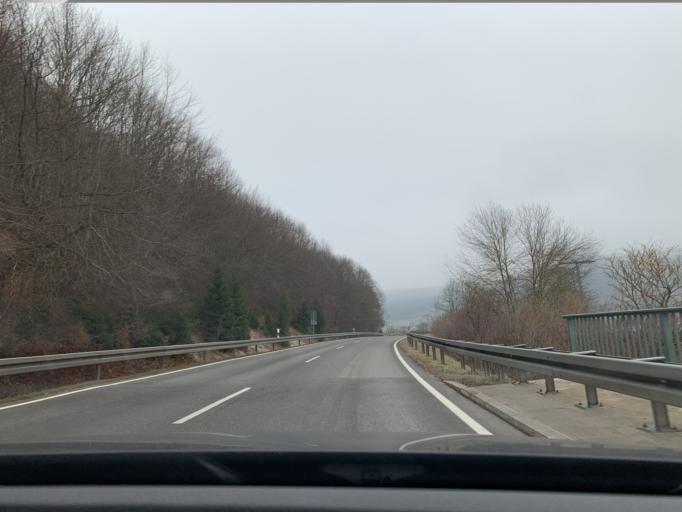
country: DE
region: Baden-Wuerttemberg
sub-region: Freiburg Region
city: Geisingen
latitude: 47.9133
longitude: 8.6737
